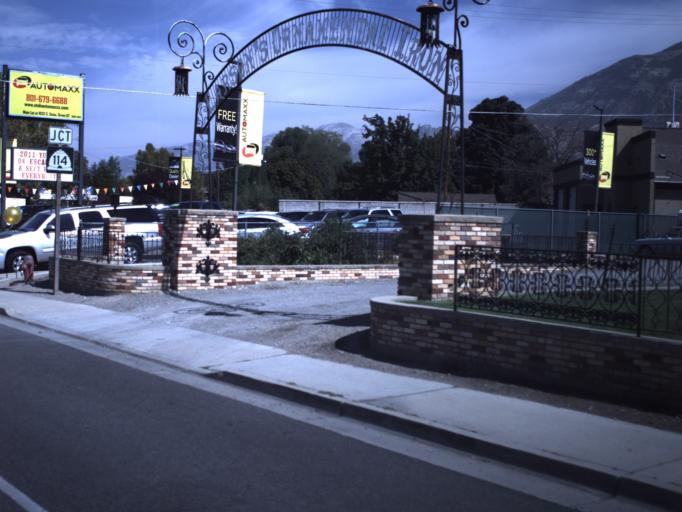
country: US
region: Utah
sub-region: Utah County
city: Pleasant Grove
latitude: 40.3569
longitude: -111.7375
